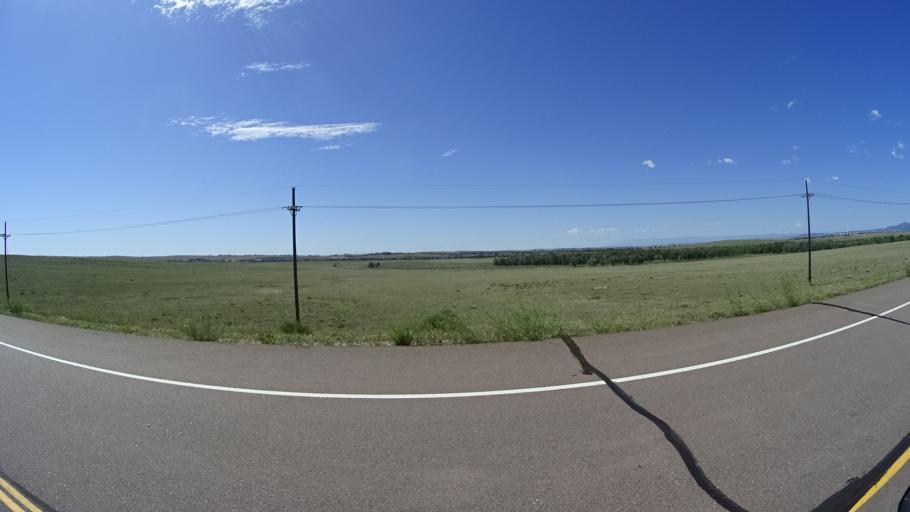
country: US
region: Colorado
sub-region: El Paso County
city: Security-Widefield
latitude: 38.7623
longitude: -104.6421
